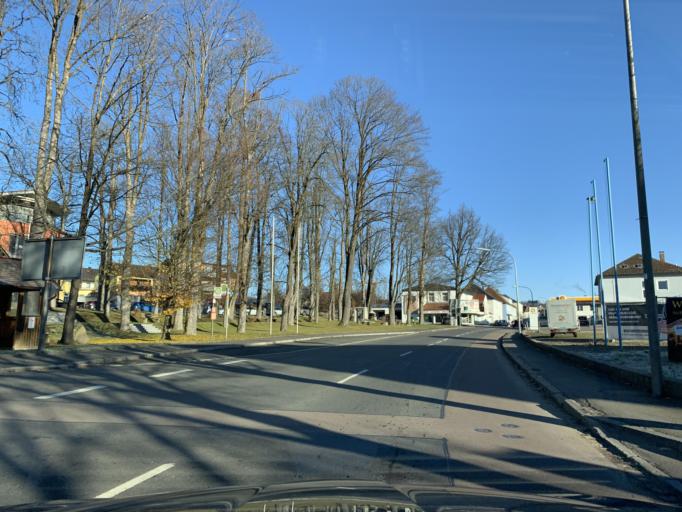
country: DE
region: Bavaria
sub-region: Upper Palatinate
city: Oberviechtach
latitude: 49.4559
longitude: 12.4164
